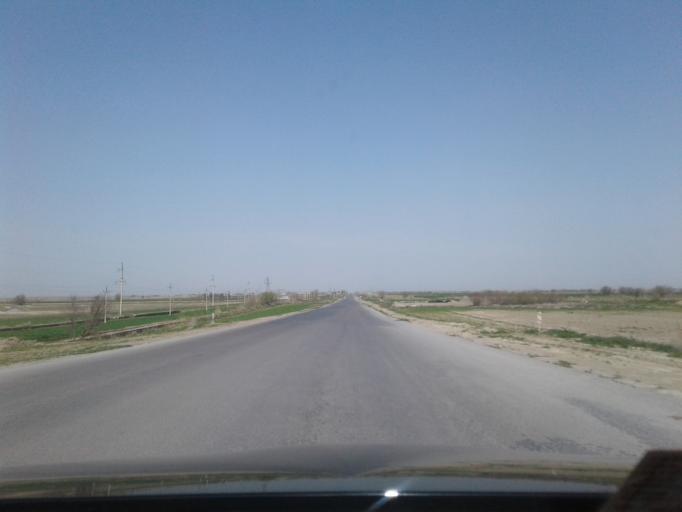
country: TM
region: Ahal
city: Abadan
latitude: 38.1918
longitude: 57.9731
